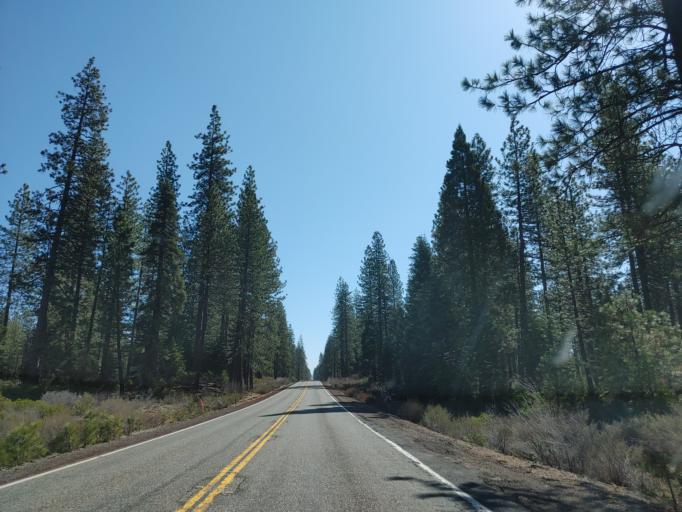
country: US
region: California
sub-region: Siskiyou County
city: McCloud
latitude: 41.2562
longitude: -122.0391
